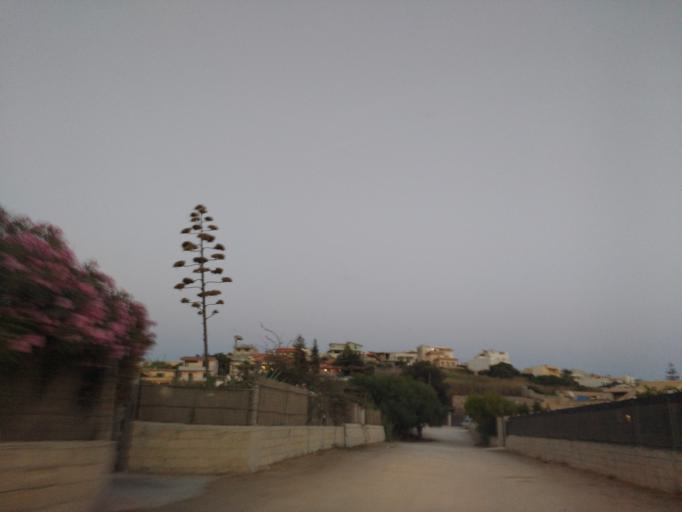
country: IT
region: Sicily
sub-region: Ragusa
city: Cava d'Aliga
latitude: 36.7345
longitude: 14.6805
